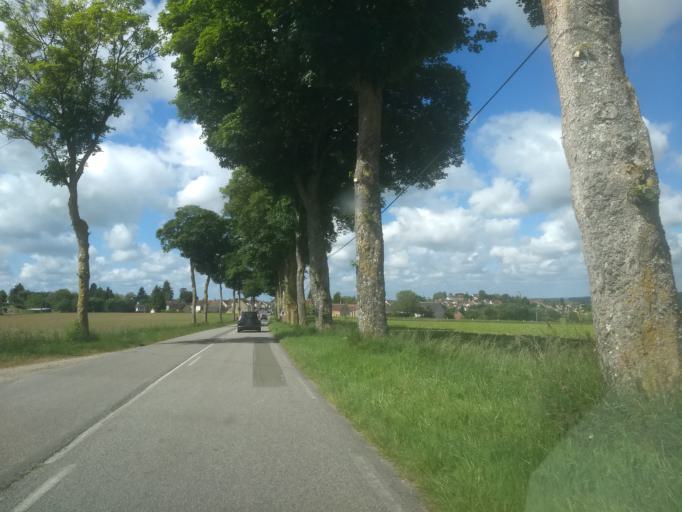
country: FR
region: Lower Normandy
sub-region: Departement de l'Orne
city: Belleme
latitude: 48.3774
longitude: 0.5780
